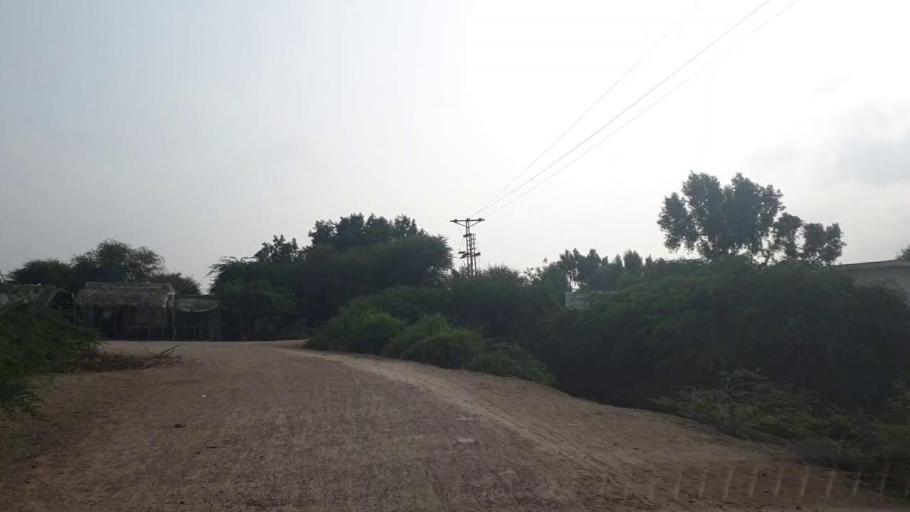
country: PK
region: Sindh
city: Badin
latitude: 24.6115
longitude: 68.6853
